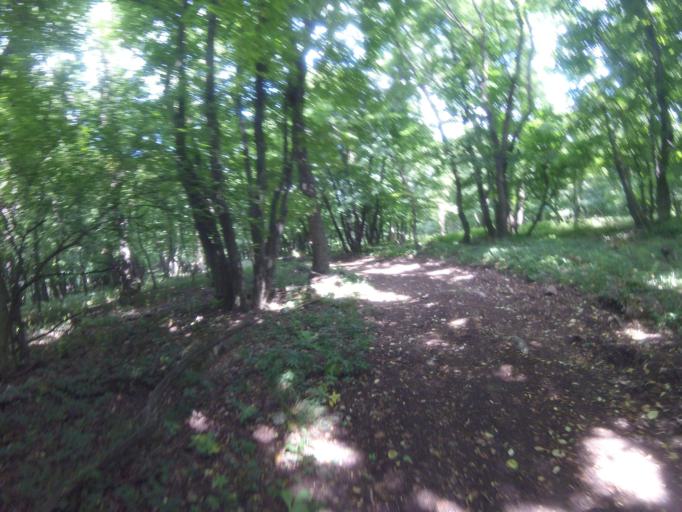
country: HU
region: Fejer
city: Szarliget
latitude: 47.4887
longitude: 18.4661
